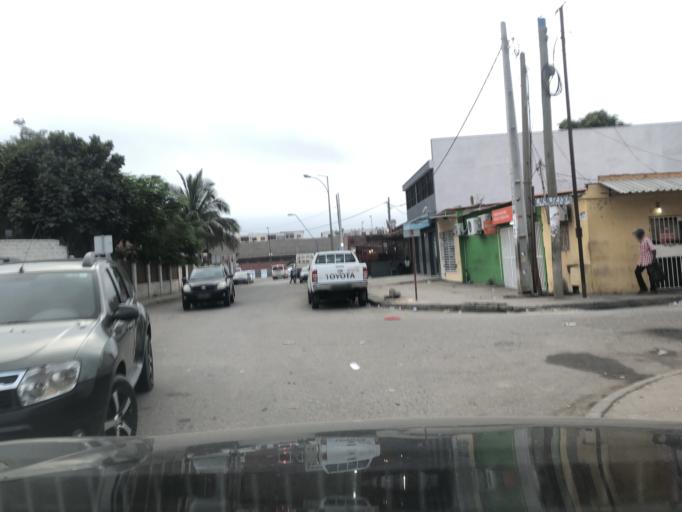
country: AO
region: Luanda
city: Luanda
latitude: -8.8425
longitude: 13.2317
